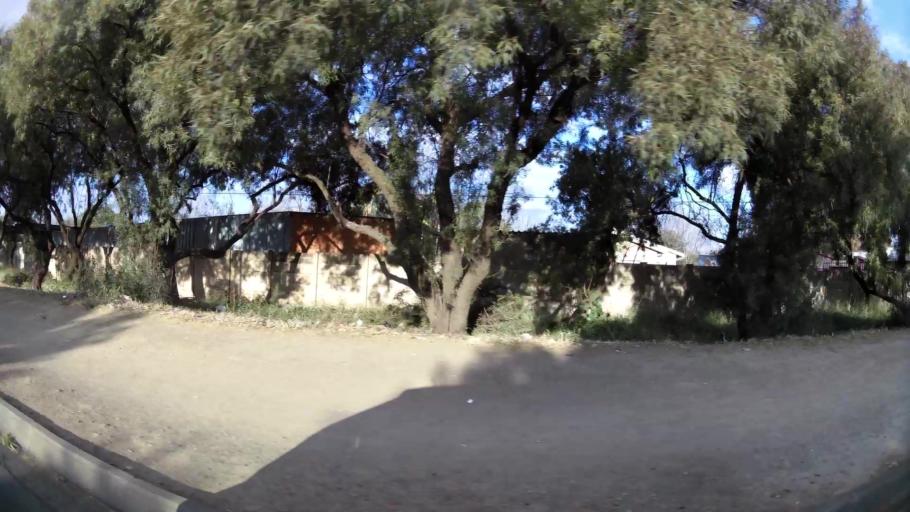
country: ZA
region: Orange Free State
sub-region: Mangaung Metropolitan Municipality
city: Bloemfontein
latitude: -29.1002
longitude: 26.1870
